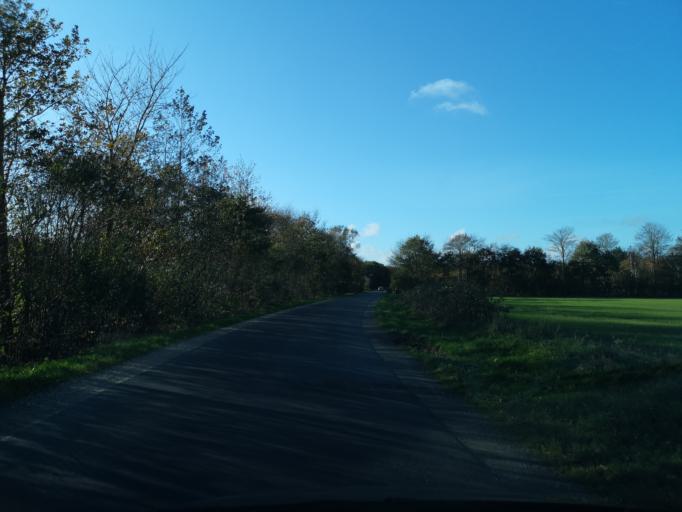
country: DK
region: Central Jutland
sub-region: Ringkobing-Skjern Kommune
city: Tarm
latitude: 55.8171
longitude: 8.4174
